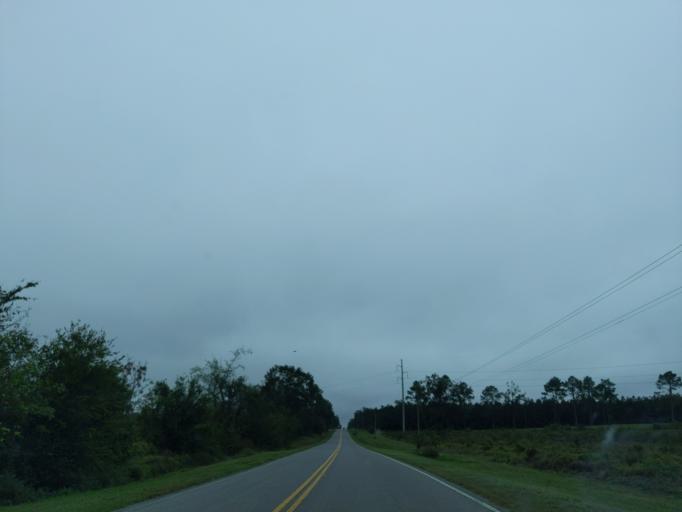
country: US
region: Florida
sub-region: Jackson County
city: Sneads
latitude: 30.6747
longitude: -84.9354
